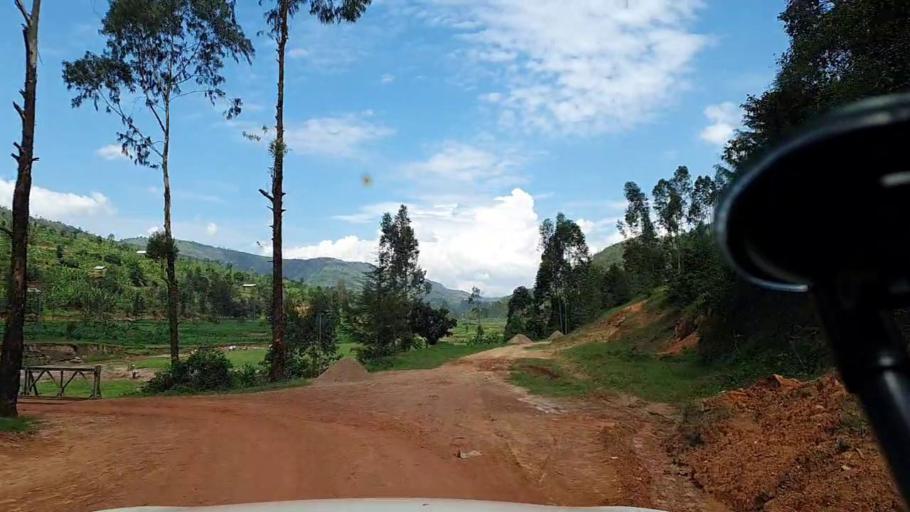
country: RW
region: Kigali
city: Kigali
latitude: -1.7922
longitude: 29.8863
